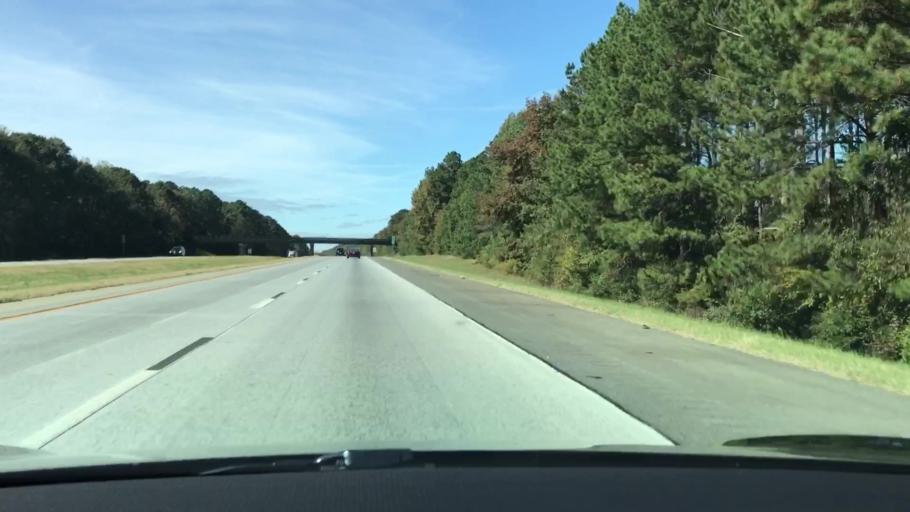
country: US
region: Georgia
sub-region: Morgan County
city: Madison
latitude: 33.5552
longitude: -83.4286
